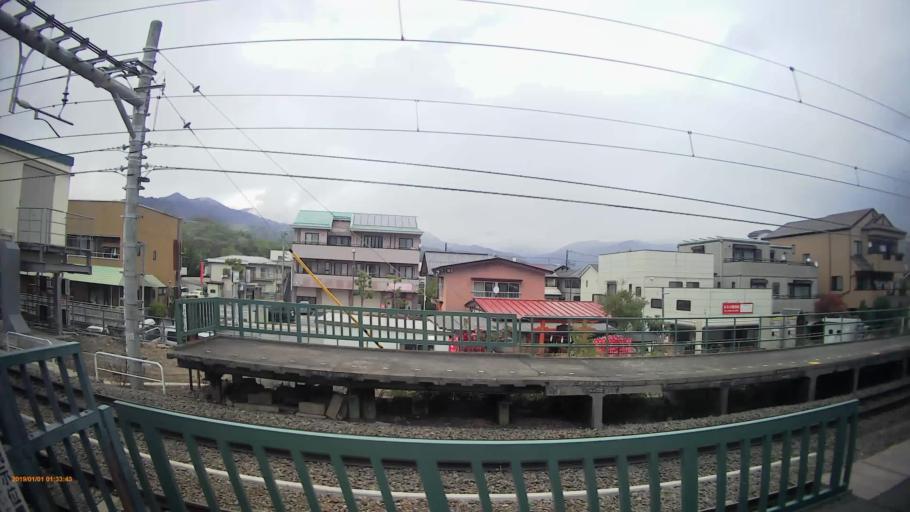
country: JP
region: Yamanashi
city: Enzan
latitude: 35.6853
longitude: 138.6818
